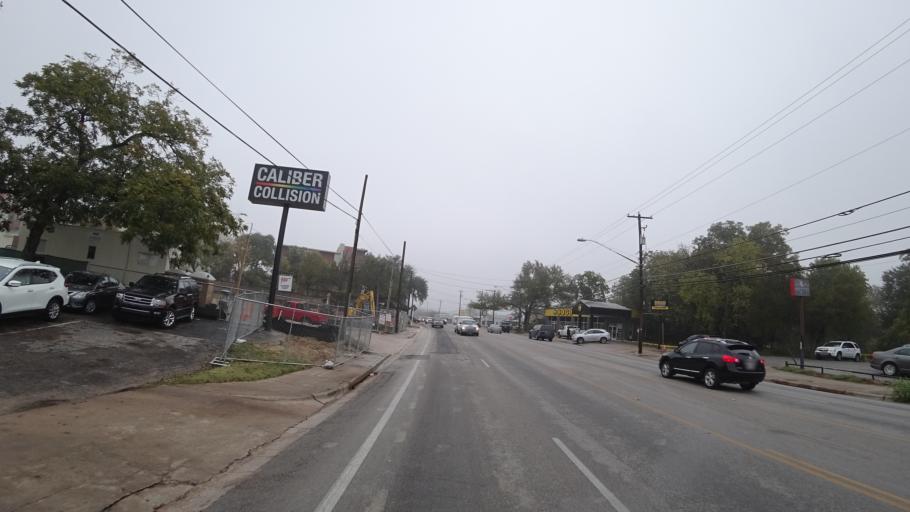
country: US
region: Texas
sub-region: Travis County
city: Austin
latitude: 30.2500
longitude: -97.7667
